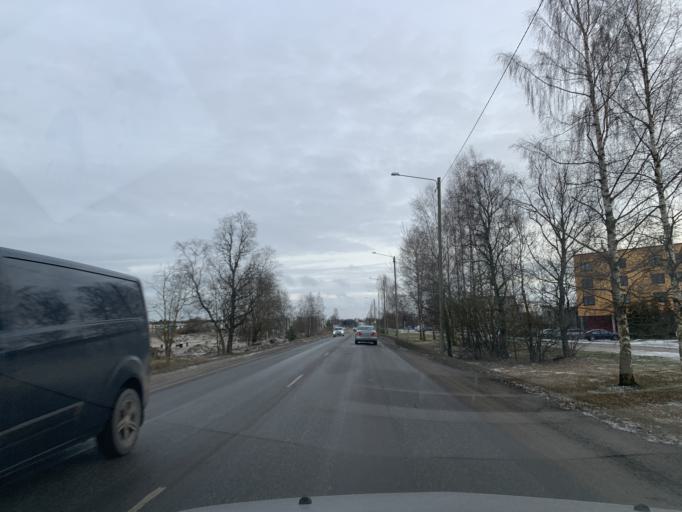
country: EE
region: Harju
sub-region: Harku vald
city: Tabasalu
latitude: 59.4306
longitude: 24.6076
